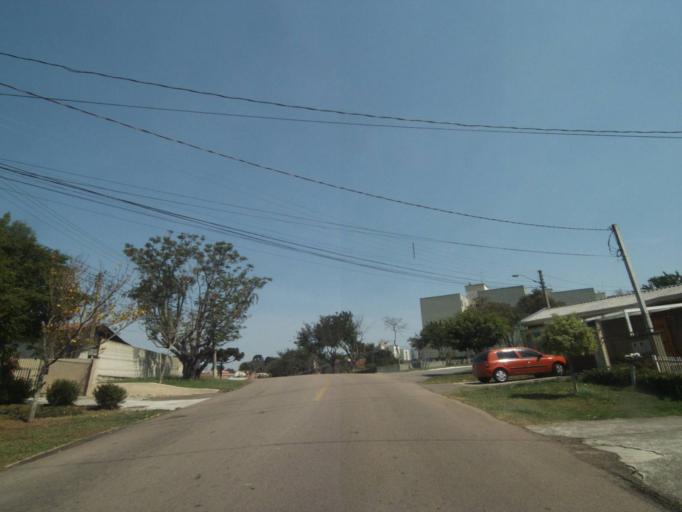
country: BR
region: Parana
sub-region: Curitiba
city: Curitiba
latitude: -25.4800
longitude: -49.2862
